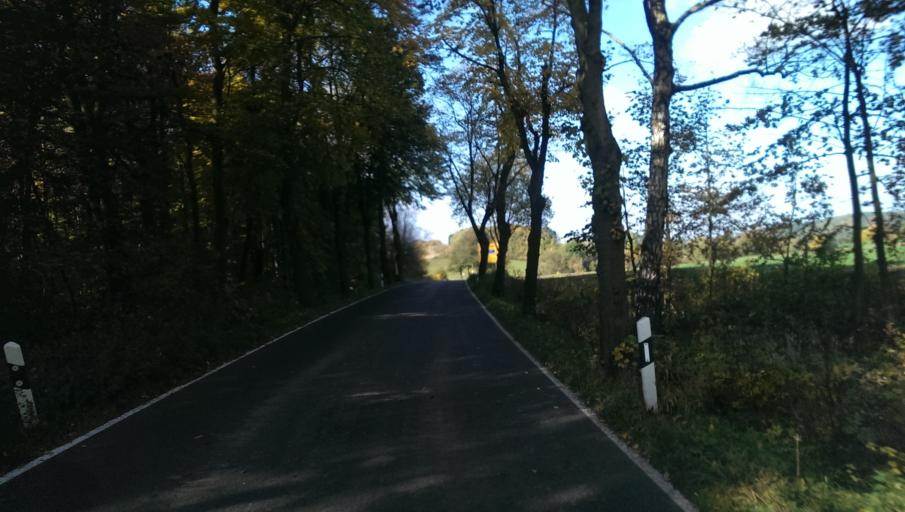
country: DE
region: Saxony
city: Dohma
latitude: 50.8316
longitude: 13.9490
